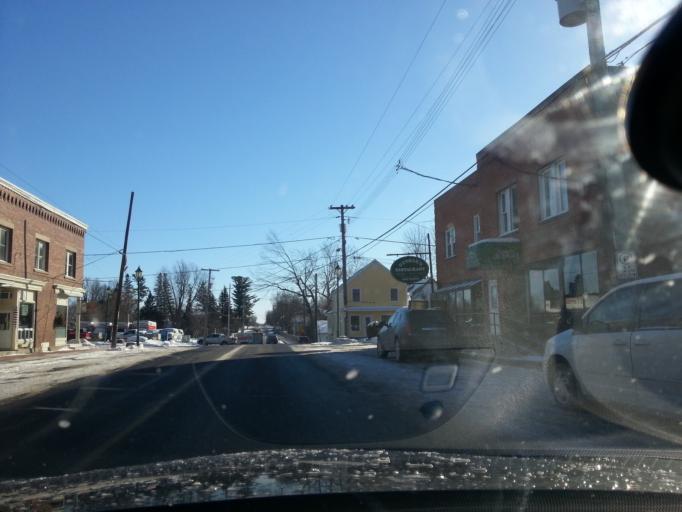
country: CA
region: Ontario
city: Bourget
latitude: 45.2571
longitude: -75.3582
